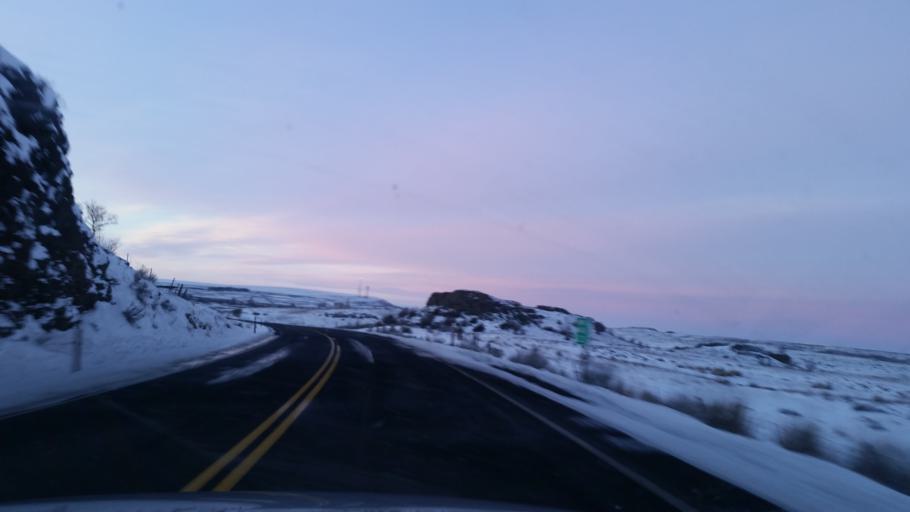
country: US
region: Washington
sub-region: Spokane County
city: Medical Lake
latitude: 47.2866
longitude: -117.9628
